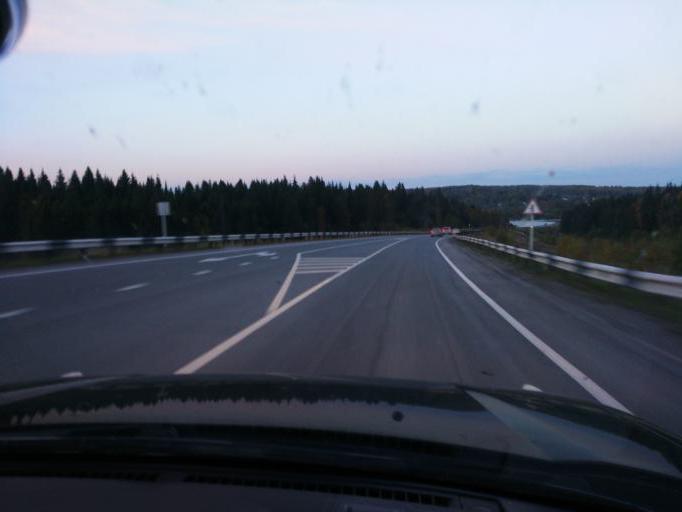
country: RU
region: Perm
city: Sylva
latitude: 58.2941
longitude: 56.8399
